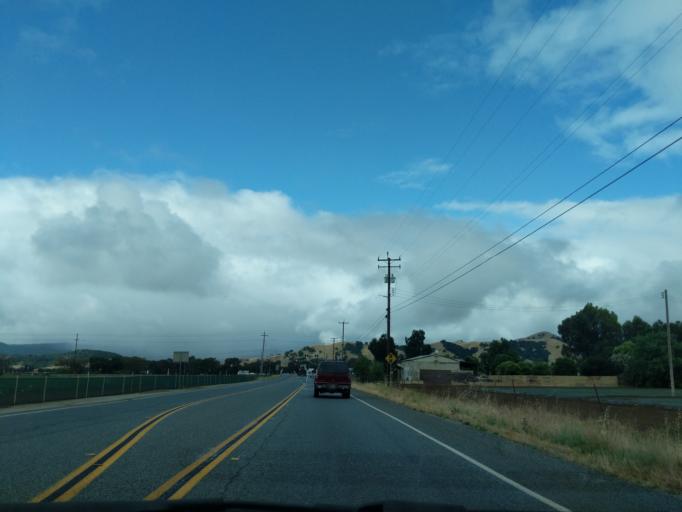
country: US
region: California
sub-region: Santa Clara County
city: San Martin
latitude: 37.0570
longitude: -121.5912
